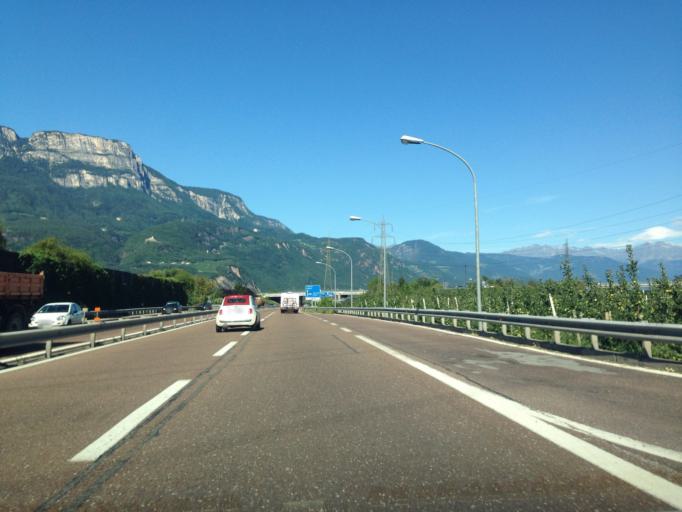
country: IT
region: Trentino-Alto Adige
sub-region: Bolzano
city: Cornaiano
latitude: 46.4846
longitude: 11.2939
